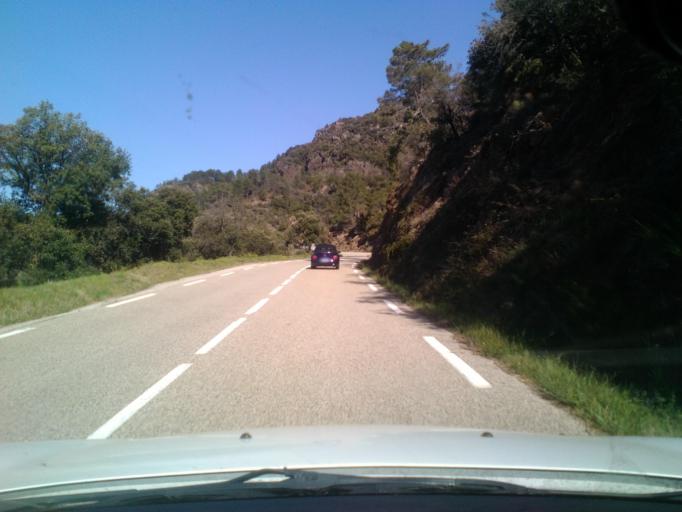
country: FR
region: Languedoc-Roussillon
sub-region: Departement du Gard
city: Saint-Jean-du-Gard
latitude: 44.1325
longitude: 3.8486
